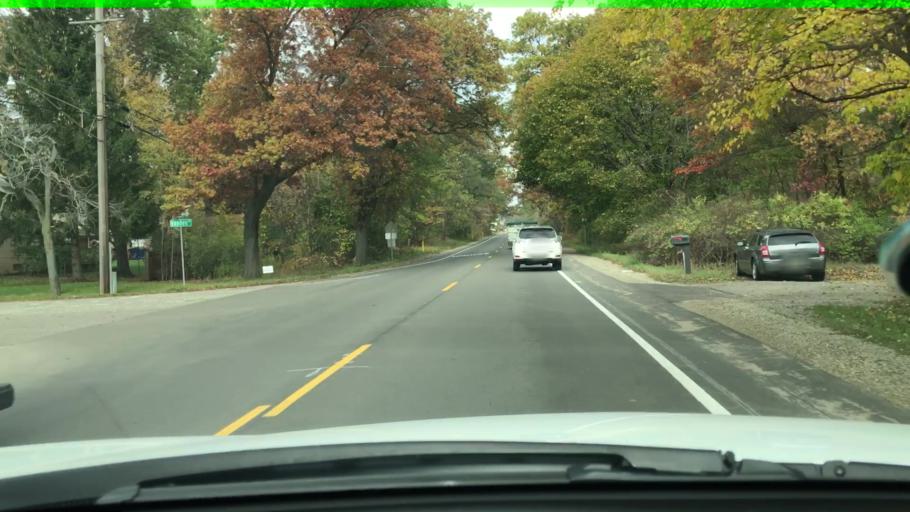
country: US
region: Michigan
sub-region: Oakland County
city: Waterford
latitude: 42.6486
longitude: -83.4435
